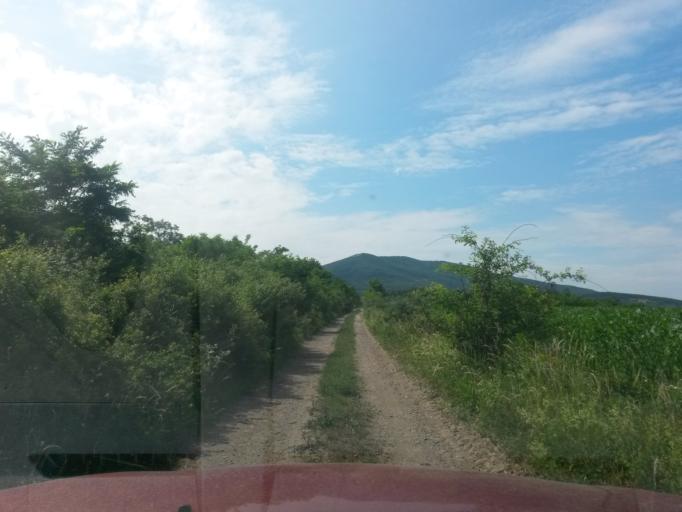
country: SK
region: Kosicky
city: Secovce
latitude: 48.6258
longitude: 21.5021
